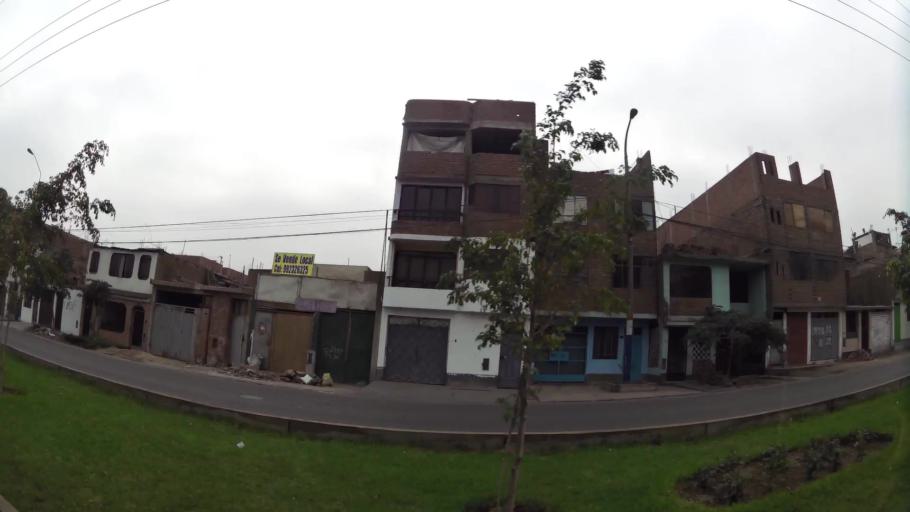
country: PE
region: Lima
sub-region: Lima
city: Independencia
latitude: -11.9681
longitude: -76.9894
